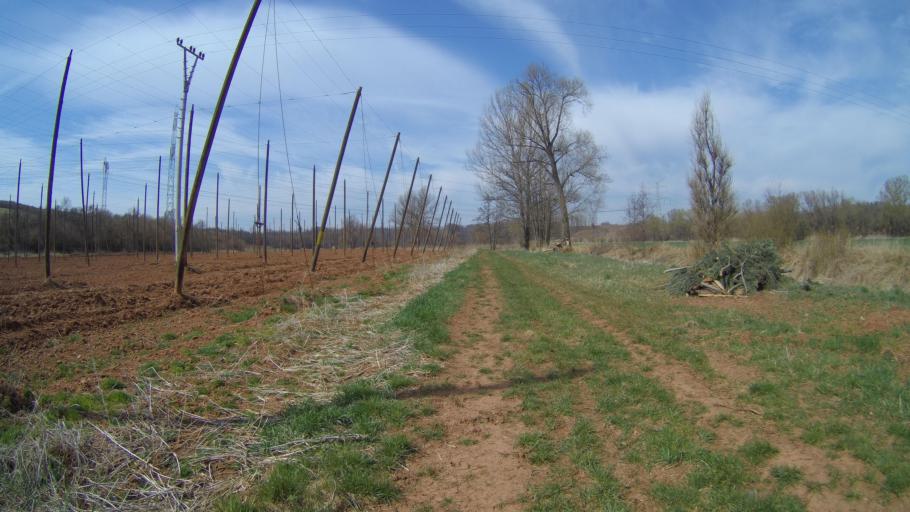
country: CZ
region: Ustecky
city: Mecholupy
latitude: 50.2303
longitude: 13.4906
